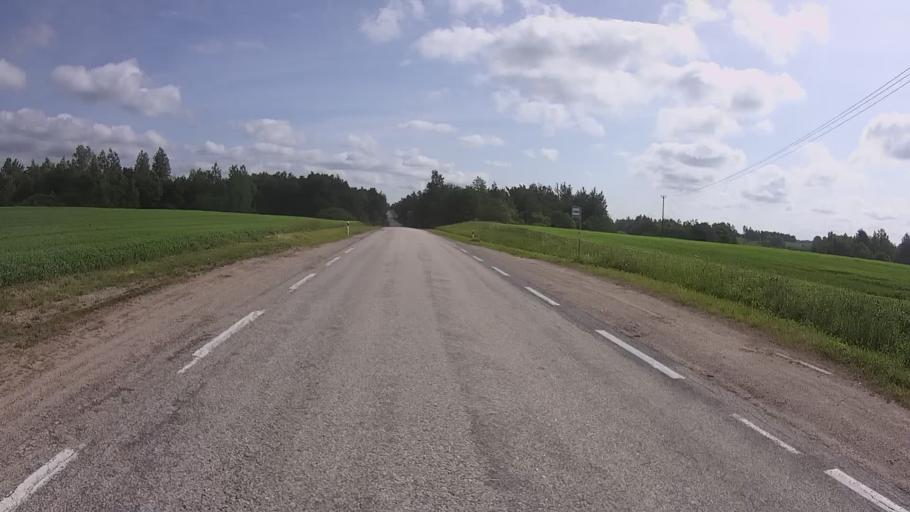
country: EE
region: Vorumaa
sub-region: Antsla vald
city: Vana-Antsla
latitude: 57.8521
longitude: 26.5855
